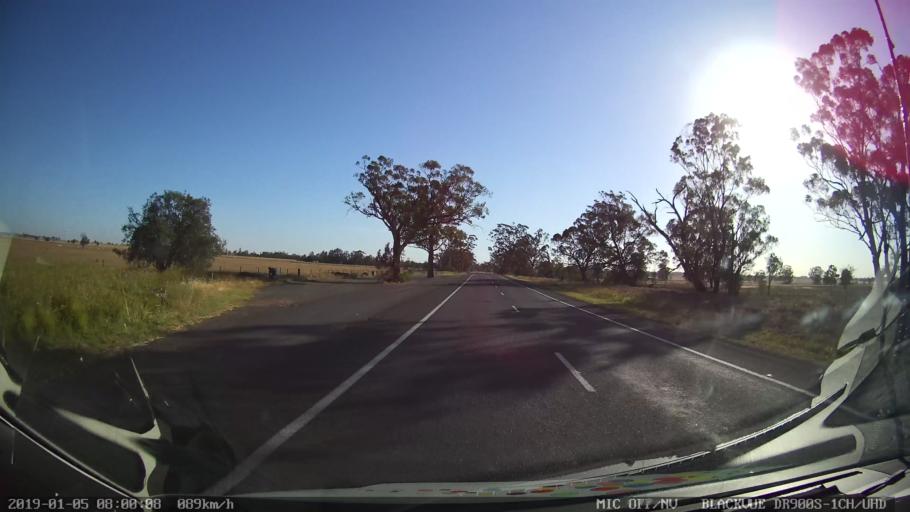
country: AU
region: New South Wales
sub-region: Gilgandra
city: Gilgandra
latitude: -31.6952
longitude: 148.6841
